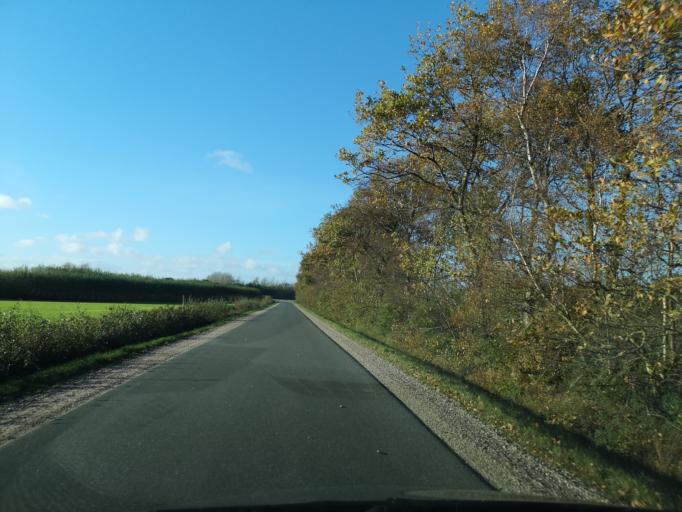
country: DK
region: Central Jutland
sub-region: Ringkobing-Skjern Kommune
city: Tarm
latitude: 55.8151
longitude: 8.4297
